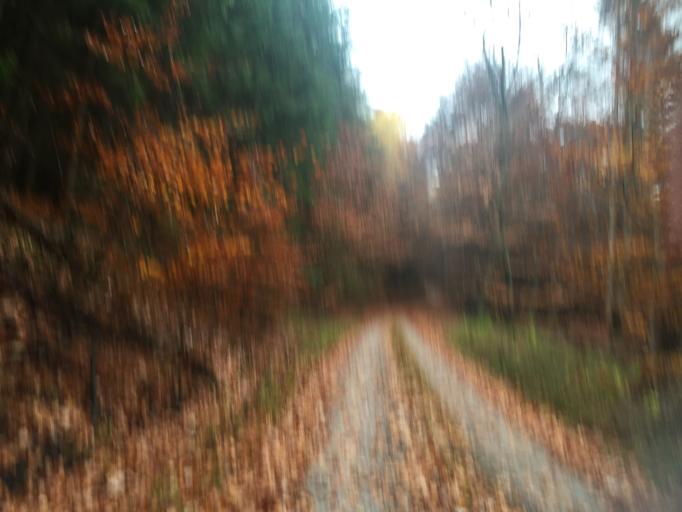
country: DE
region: Baden-Wuerttemberg
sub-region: Karlsruhe Region
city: Heddesbach
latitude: 49.4634
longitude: 8.8457
